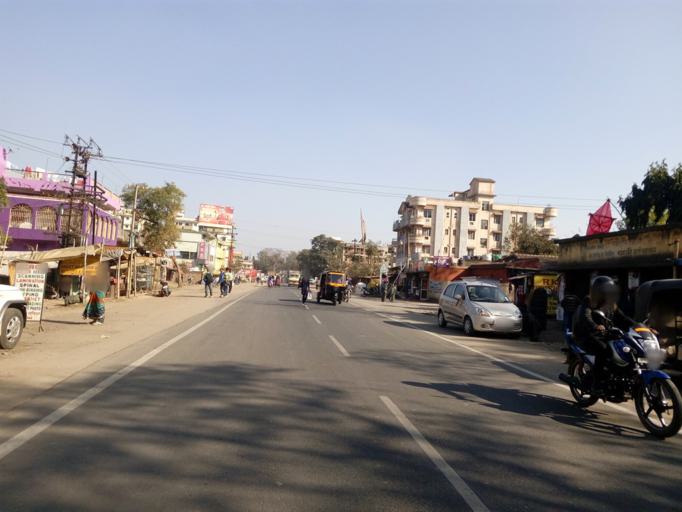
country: IN
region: Jharkhand
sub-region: Ranchi
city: Ranchi
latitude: 23.3609
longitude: 85.3548
